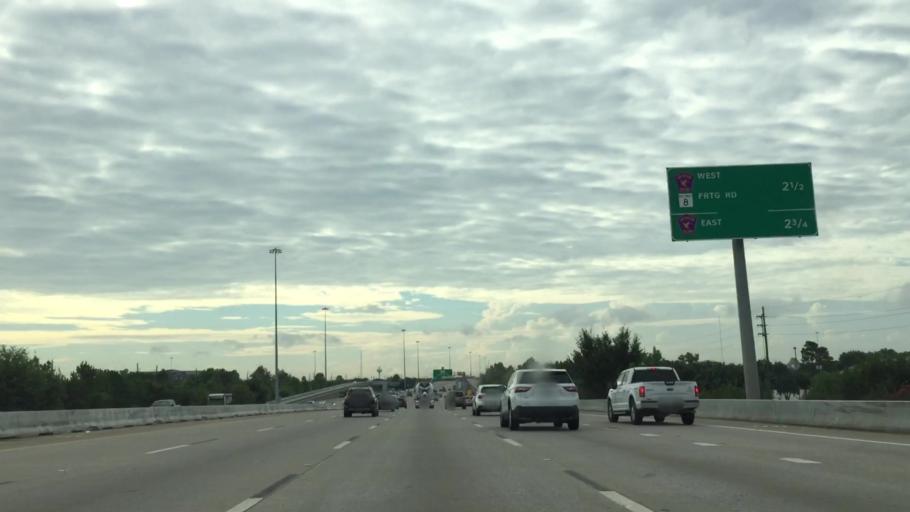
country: US
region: Texas
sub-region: Harris County
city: Jersey Village
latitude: 29.9664
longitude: -95.5557
